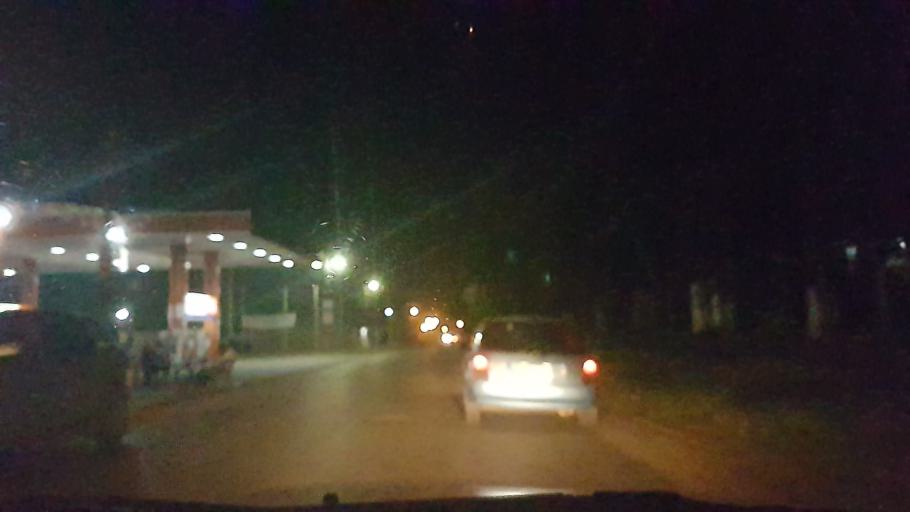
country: PY
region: Central
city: Colonia Mariano Roque Alonso
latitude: -25.1881
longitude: -57.5266
